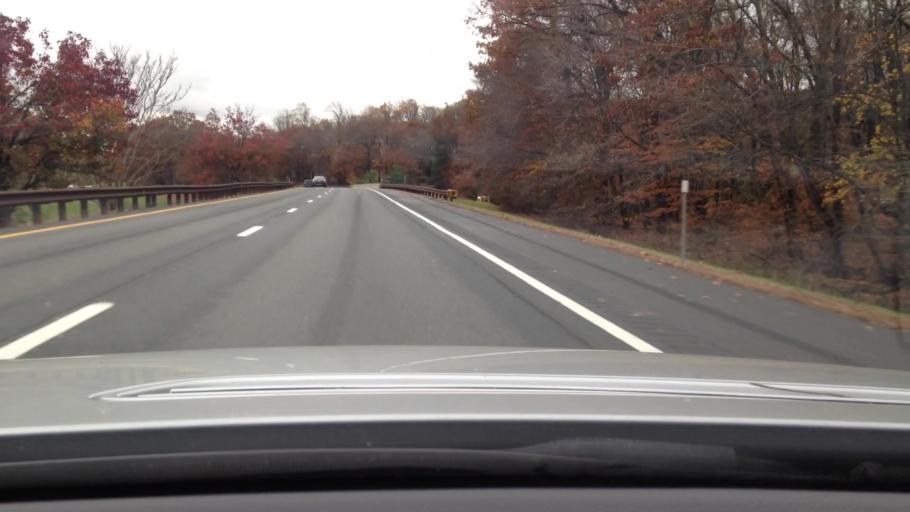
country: US
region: New Jersey
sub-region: Bergen County
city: Woodcliff Lake
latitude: 41.0263
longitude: -74.0701
